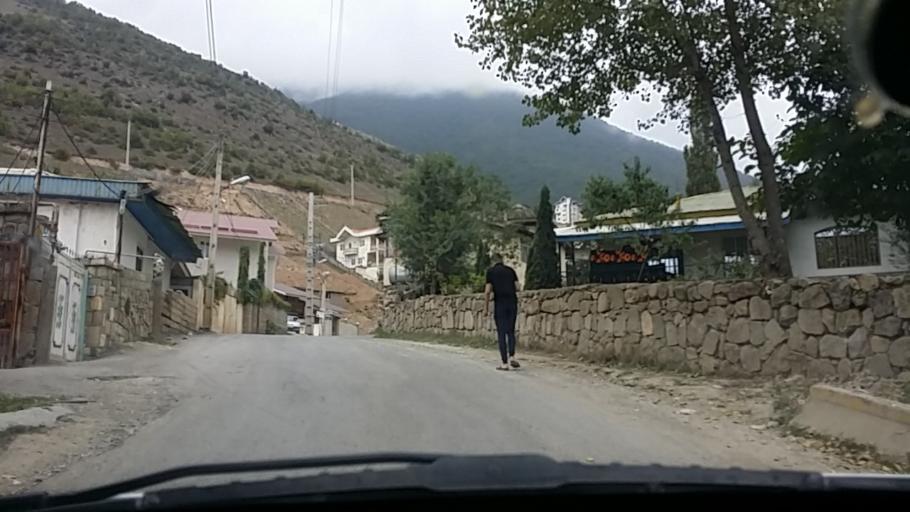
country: IR
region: Mazandaran
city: `Abbasabad
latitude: 36.4788
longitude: 51.1388
